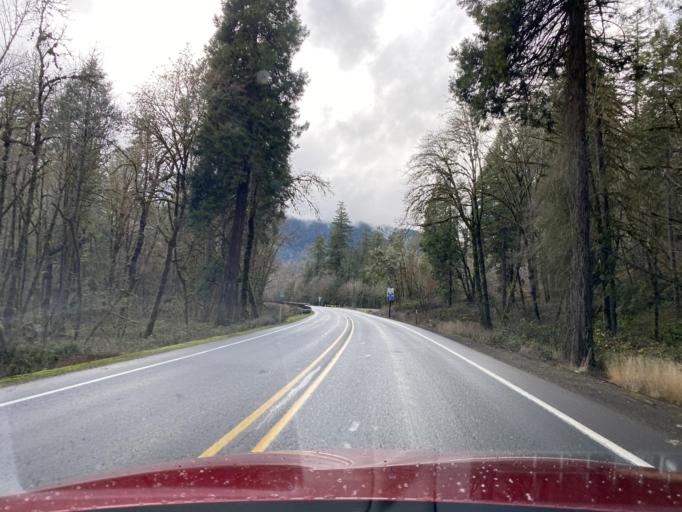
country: US
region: Oregon
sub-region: Lane County
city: Oakridge
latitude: 43.7481
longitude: -122.5067
